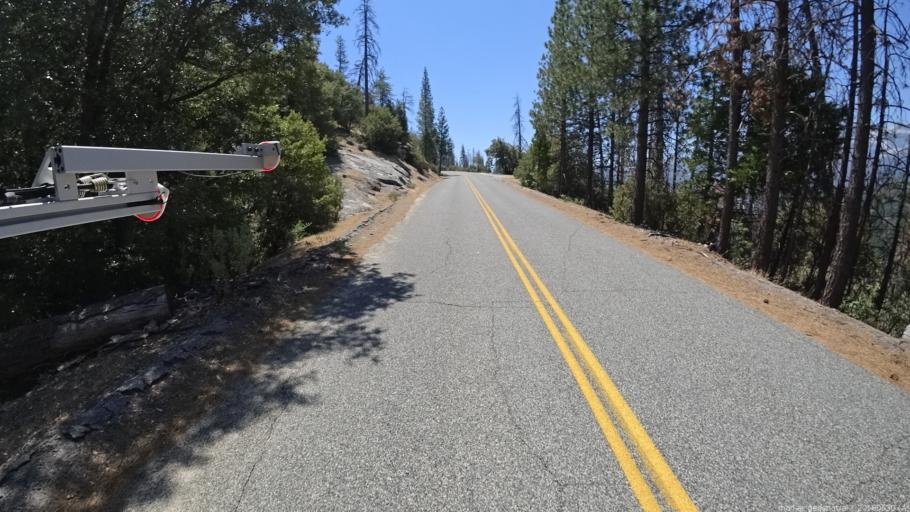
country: US
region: California
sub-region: Madera County
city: Oakhurst
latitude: 37.3854
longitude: -119.3637
